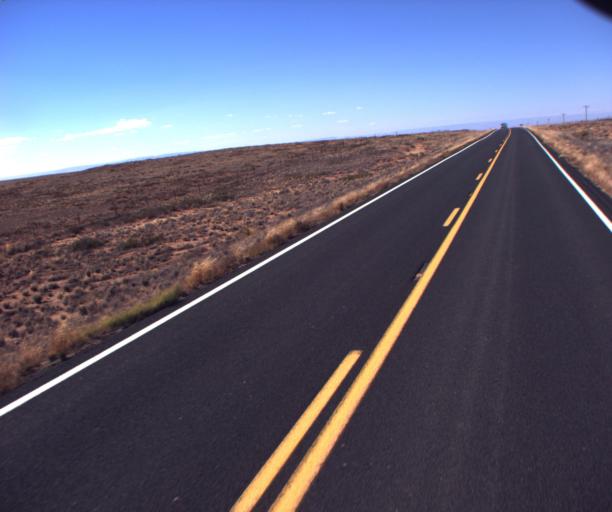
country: US
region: Arizona
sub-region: Coconino County
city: Tuba City
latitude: 36.0072
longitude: -111.0547
